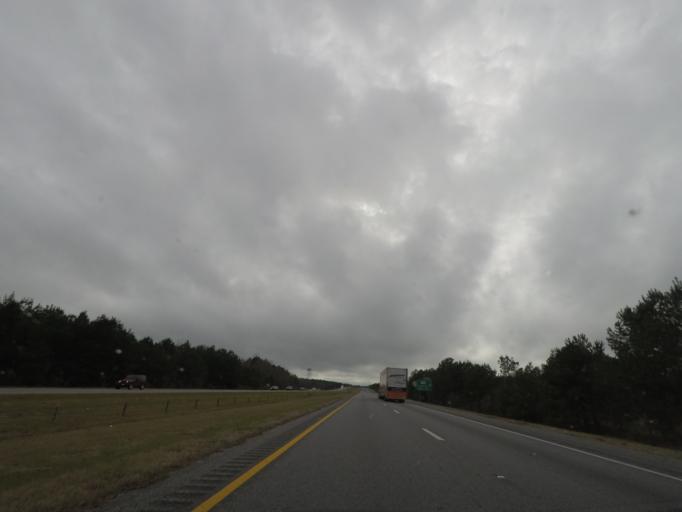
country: US
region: South Carolina
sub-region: Orangeburg County
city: Holly Hill
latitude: 33.3888
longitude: -80.5165
